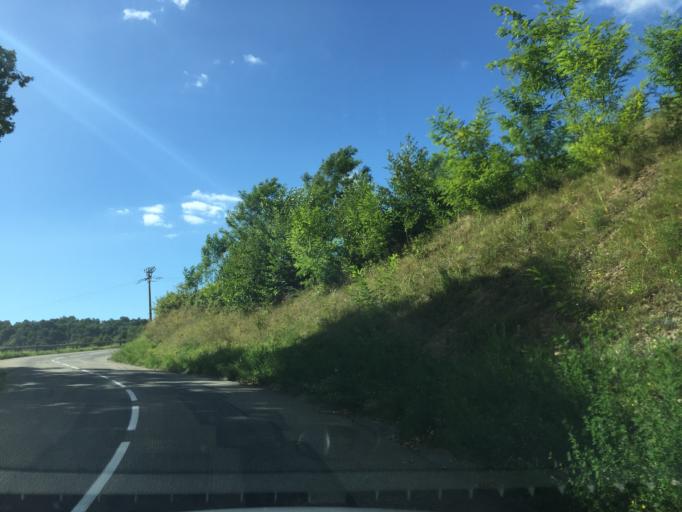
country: FR
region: Rhone-Alpes
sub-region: Departement de la Savoie
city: La Rochette
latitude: 45.4704
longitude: 6.1837
